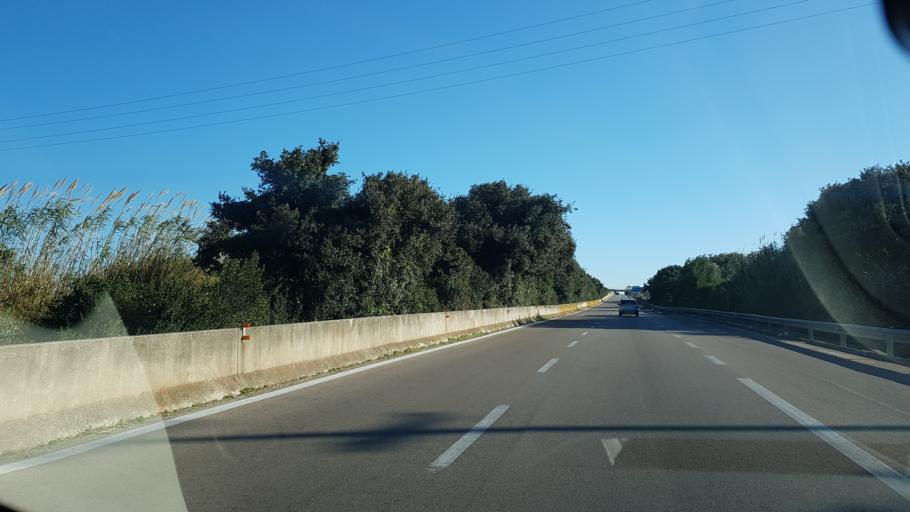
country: IT
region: Apulia
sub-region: Provincia di Lecce
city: Alezio
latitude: 40.0175
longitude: 18.0451
